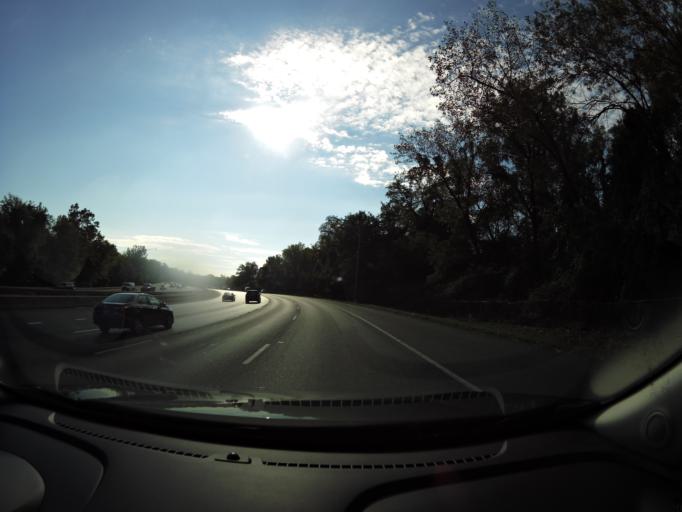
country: US
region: Maryland
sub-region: Montgomery County
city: South Kensington
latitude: 39.0123
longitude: -77.0936
